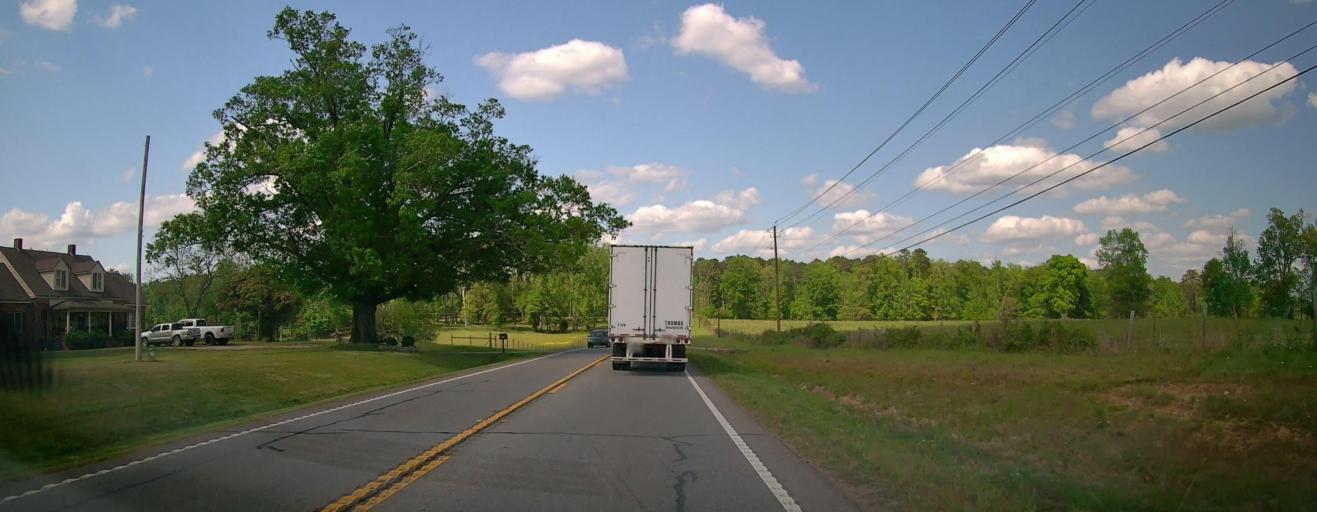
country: US
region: Georgia
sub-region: Greene County
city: Greensboro
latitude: 33.5149
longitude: -83.2257
